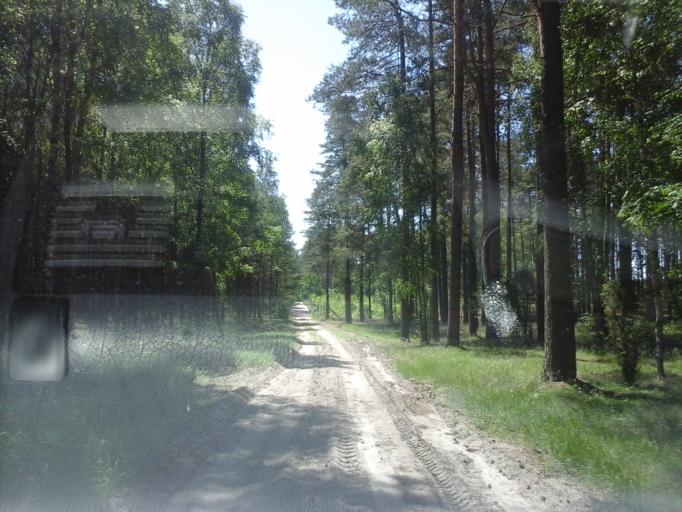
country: PL
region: West Pomeranian Voivodeship
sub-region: Powiat drawski
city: Kalisz Pomorski
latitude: 53.2337
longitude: 16.0110
